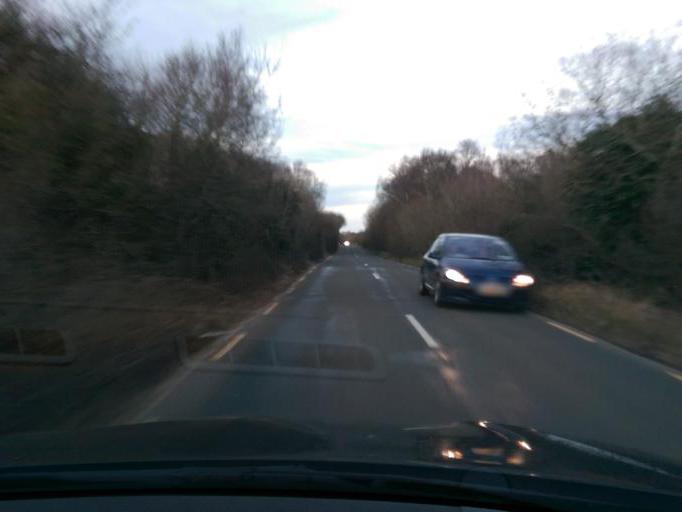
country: IE
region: Connaught
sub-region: County Galway
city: Portumna
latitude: 53.0601
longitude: -8.0944
